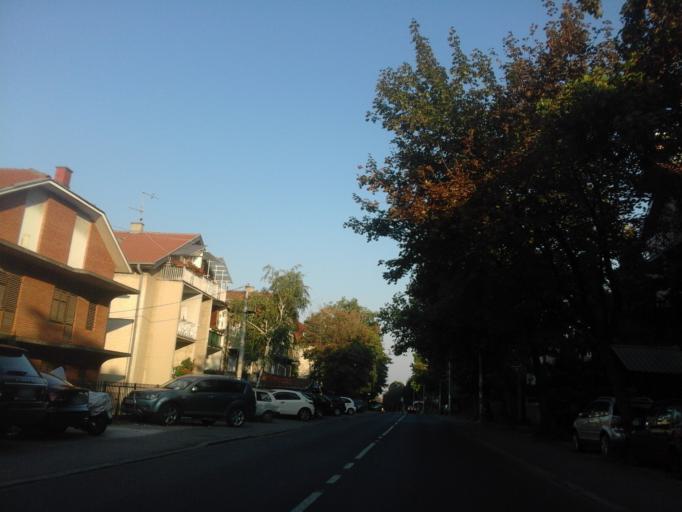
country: RS
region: Central Serbia
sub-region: Belgrade
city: Cukarica
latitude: 44.7671
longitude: 20.4222
